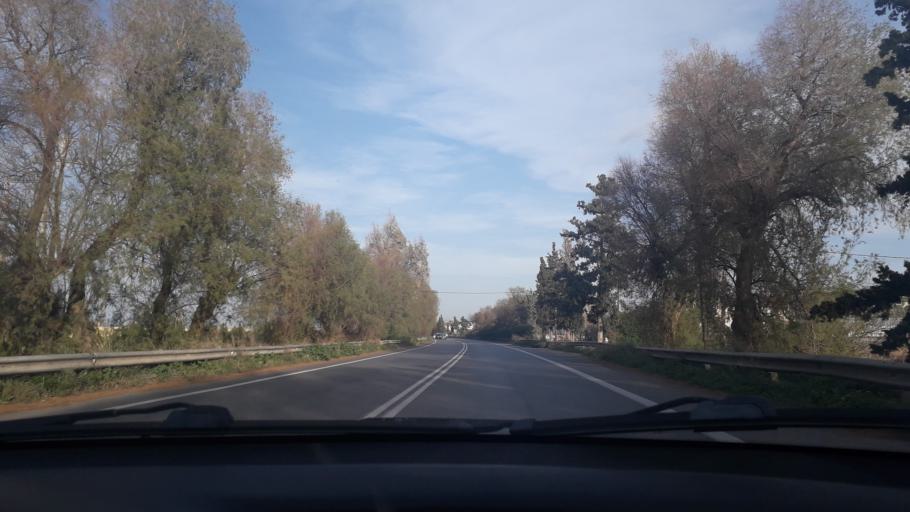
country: GR
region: Crete
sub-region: Nomos Rethymnis
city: Rethymno
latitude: 35.3727
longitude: 24.5544
